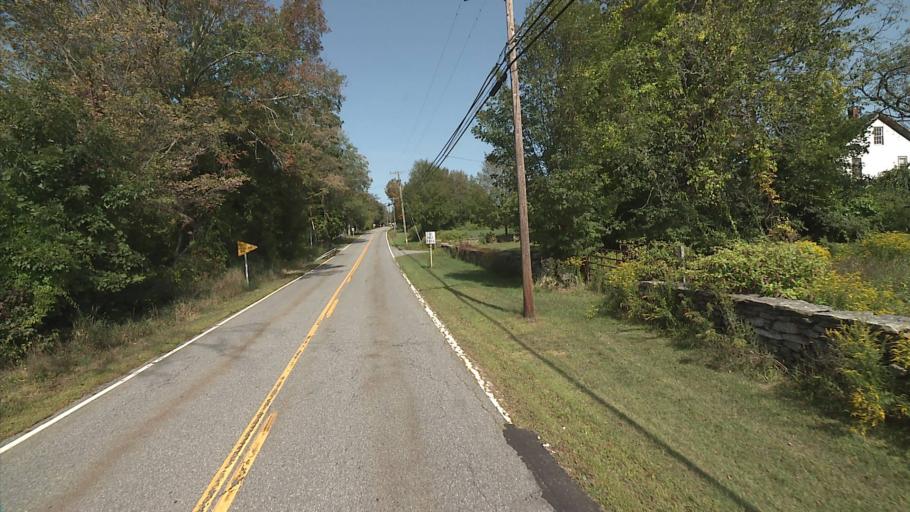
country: US
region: Connecticut
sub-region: Windham County
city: South Woodstock
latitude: 41.9667
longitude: -71.9867
